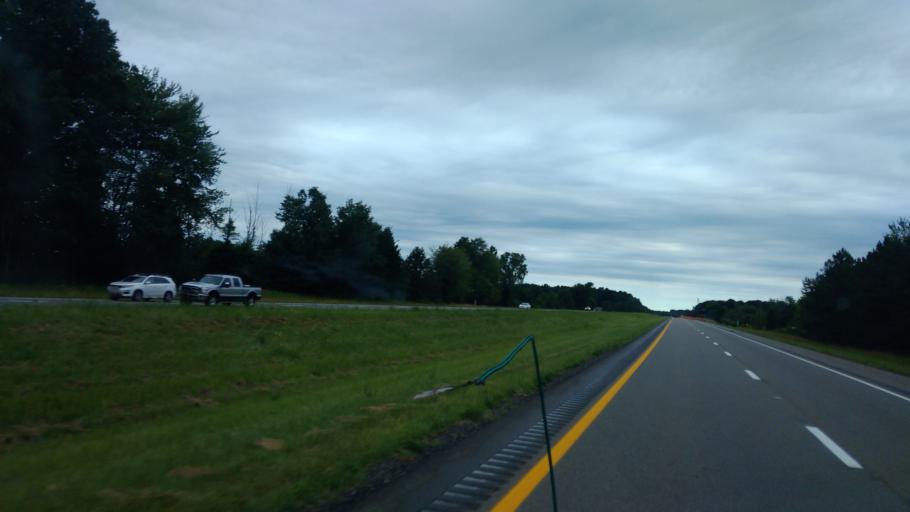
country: US
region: Ohio
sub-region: Mahoning County
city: Canfield
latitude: 40.9681
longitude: -80.7195
